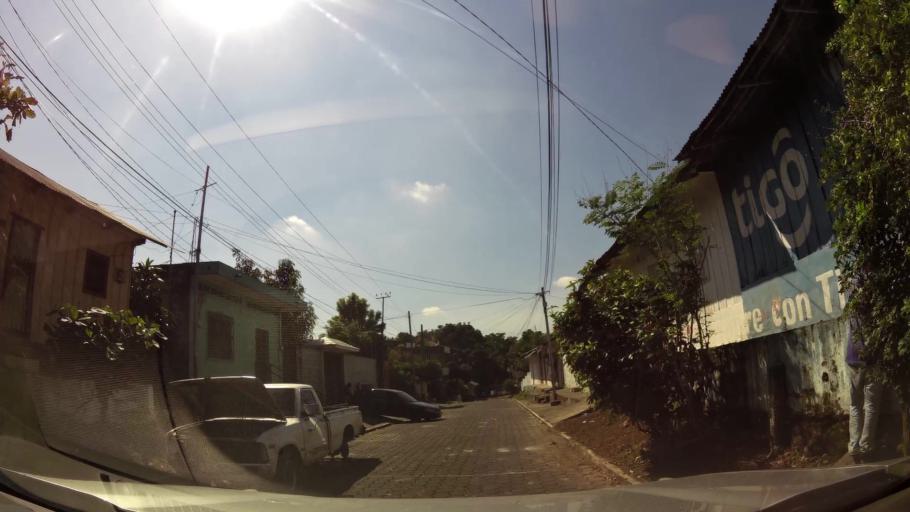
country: GT
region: Suchitepeque
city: Mazatenango
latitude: 14.5338
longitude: -91.4992
